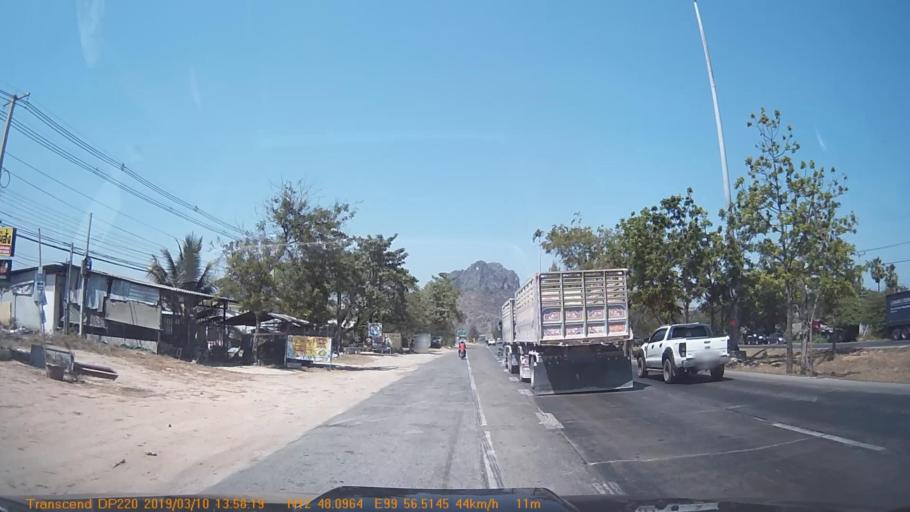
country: TH
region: Phetchaburi
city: Cha-am
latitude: 12.8016
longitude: 99.9419
